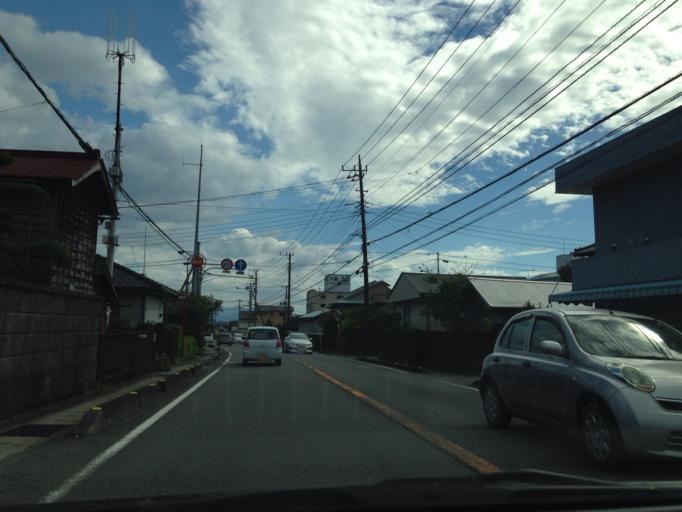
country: JP
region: Shizuoka
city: Mishima
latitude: 35.1828
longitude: 138.9090
